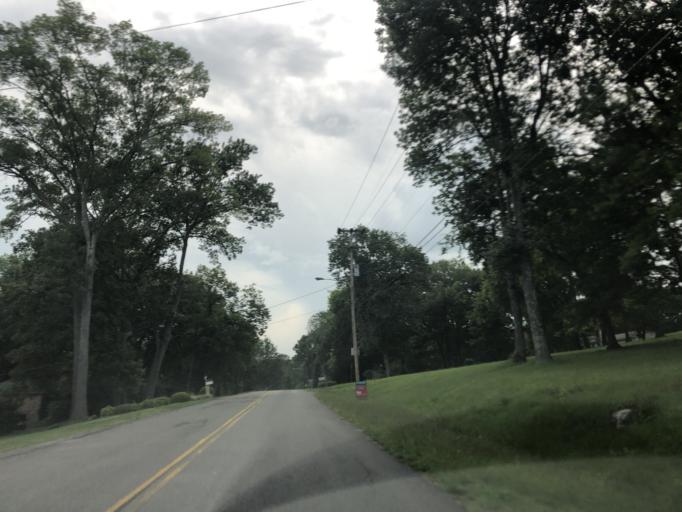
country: US
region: Tennessee
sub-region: Davidson County
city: Lakewood
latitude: 36.1831
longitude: -86.6883
